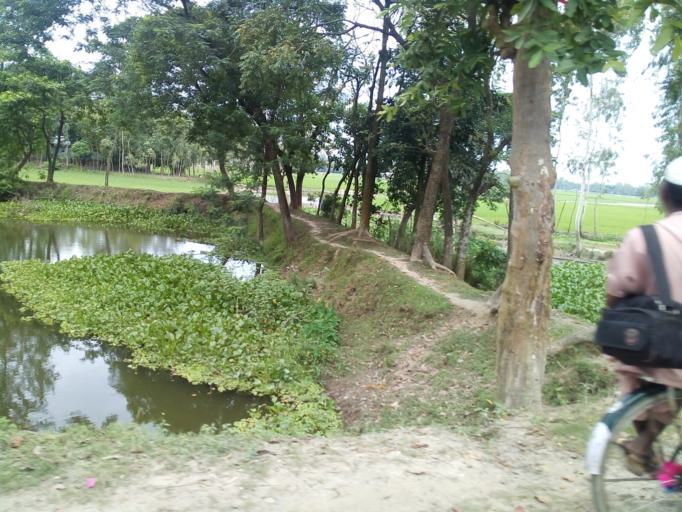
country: BD
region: Rangpur Division
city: Nageswari
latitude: 25.8907
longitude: 89.7133
